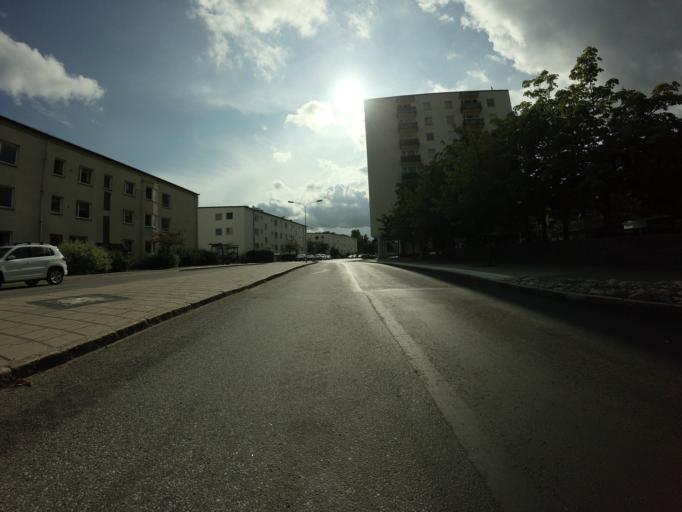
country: SE
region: Stockholm
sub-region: Lidingo
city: Lidingoe
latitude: 59.3734
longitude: 18.1446
